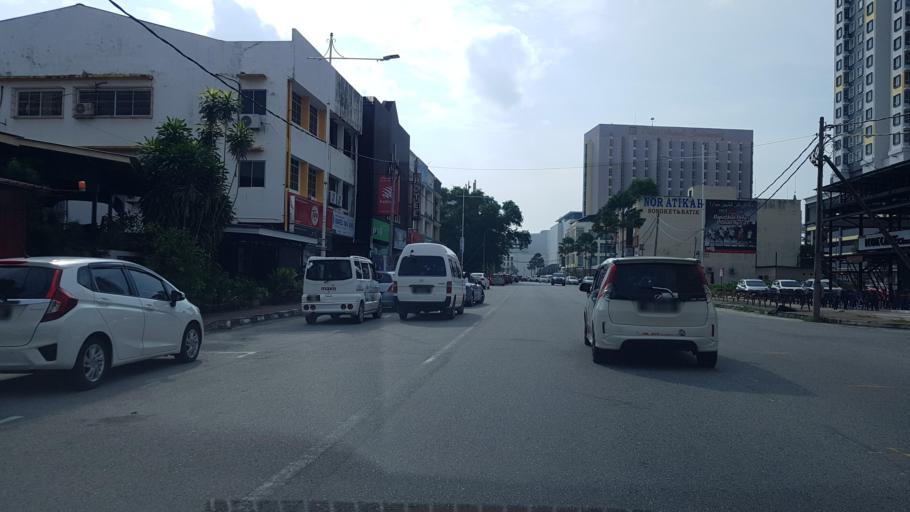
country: MY
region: Terengganu
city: Kuala Terengganu
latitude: 5.3332
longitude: 103.1479
